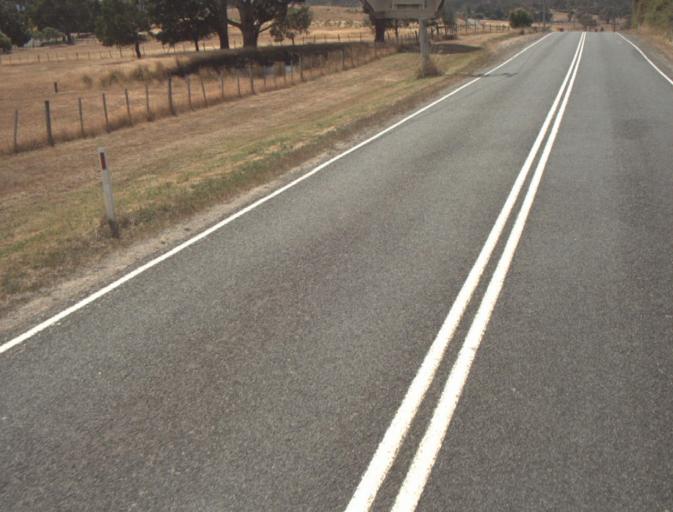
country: AU
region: Tasmania
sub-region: Launceston
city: Newstead
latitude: -41.4432
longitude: 147.2136
